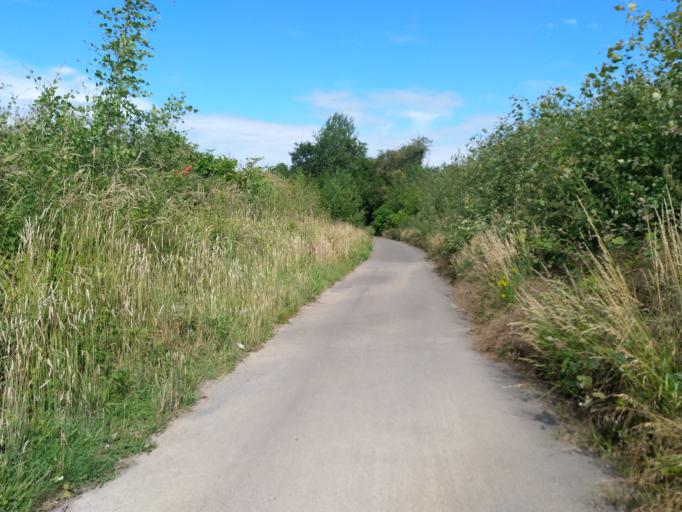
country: BE
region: Wallonia
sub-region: Province du Hainaut
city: Quievrain
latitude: 50.4116
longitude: 3.6969
